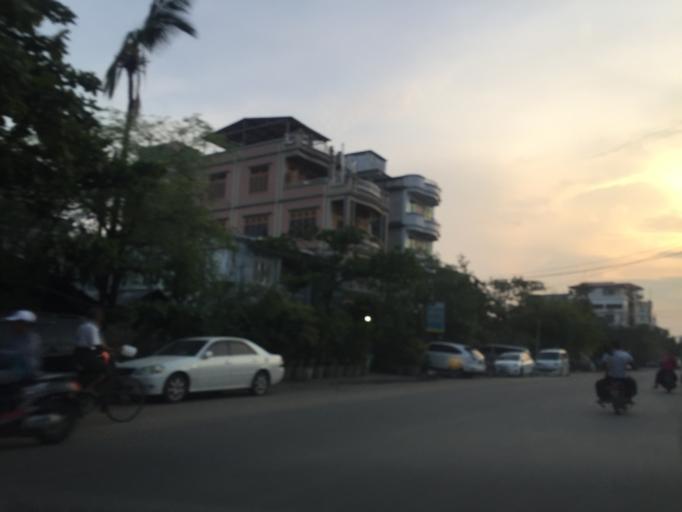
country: MM
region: Mandalay
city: Mandalay
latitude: 21.9797
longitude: 96.0920
